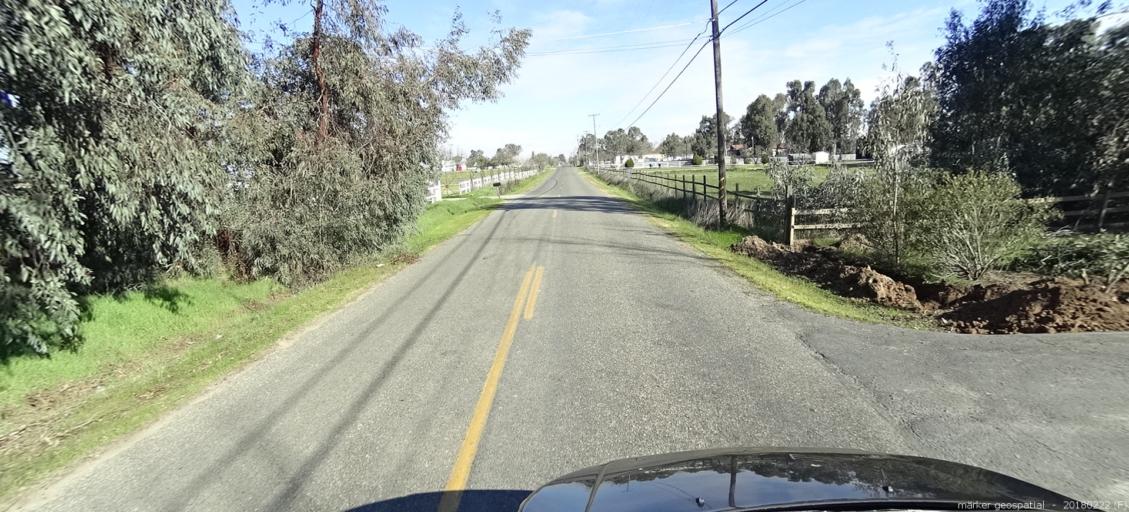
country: US
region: California
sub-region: Sacramento County
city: Elverta
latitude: 38.7197
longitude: -121.4574
